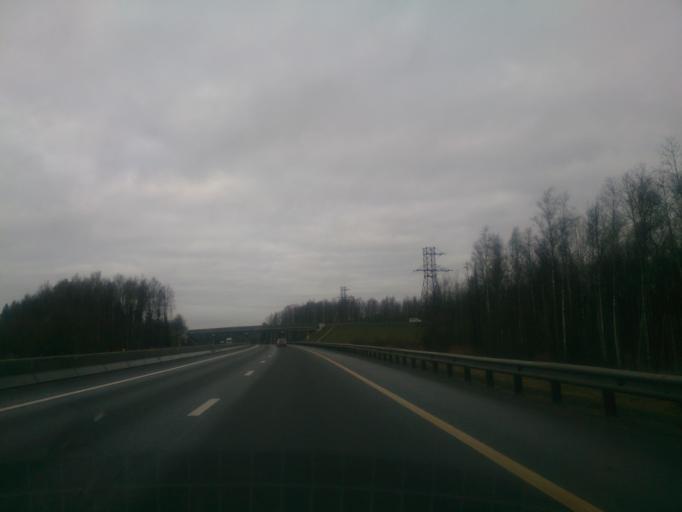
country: RU
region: Leningrad
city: Ul'yanovka
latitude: 59.5909
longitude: 30.7806
